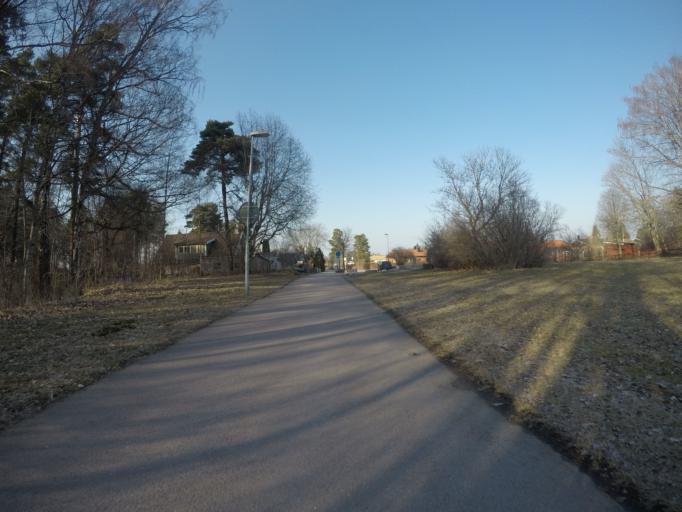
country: SE
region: Vaestmanland
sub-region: Kungsors Kommun
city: Kungsoer
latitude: 59.4232
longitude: 16.1129
